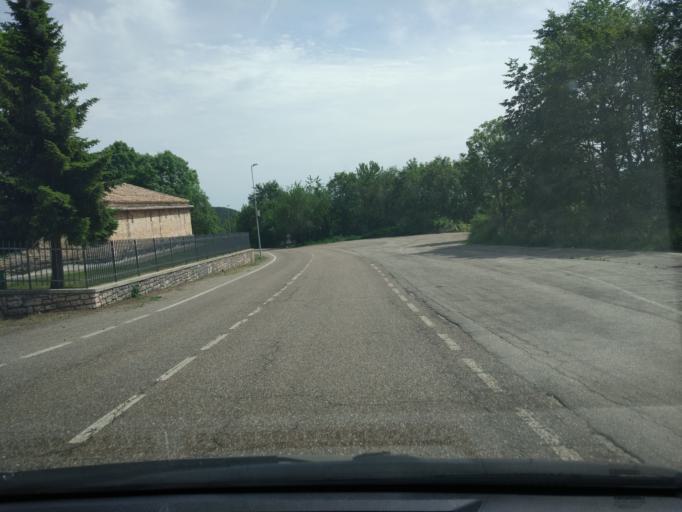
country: IT
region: Veneto
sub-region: Provincia di Verona
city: Ferrara di Monte Baldo
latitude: 45.6747
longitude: 10.8629
